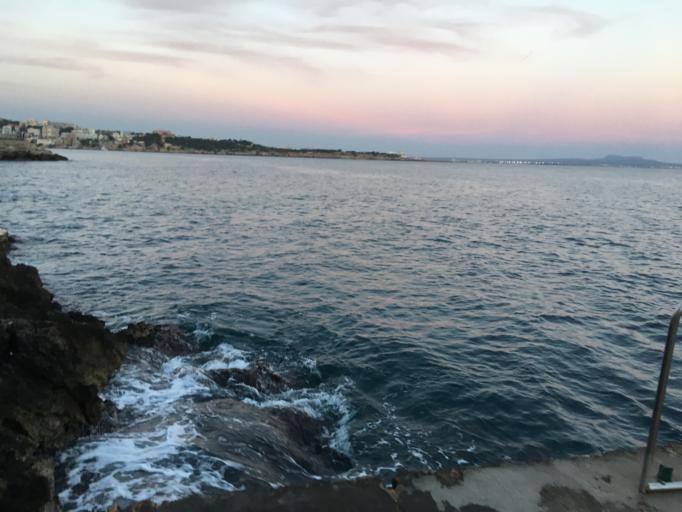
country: ES
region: Balearic Islands
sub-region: Illes Balears
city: Palma
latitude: 39.5393
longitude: 2.5936
